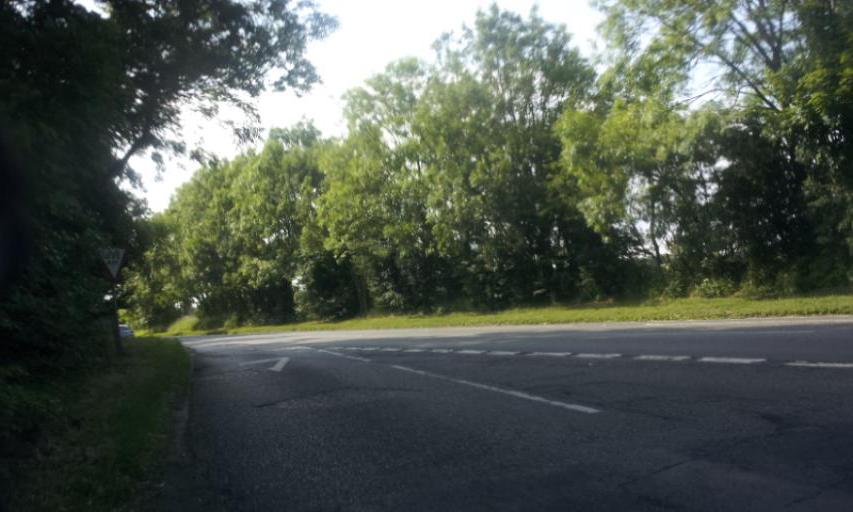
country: GB
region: England
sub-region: Kent
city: Lenham
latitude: 51.2400
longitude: 0.7101
